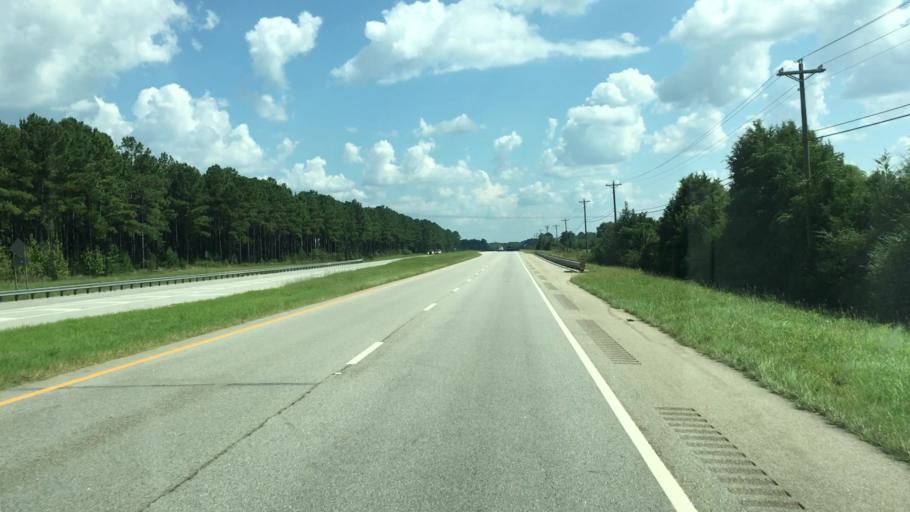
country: US
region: Georgia
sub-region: Putnam County
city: Eatonton
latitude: 33.2577
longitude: -83.3310
